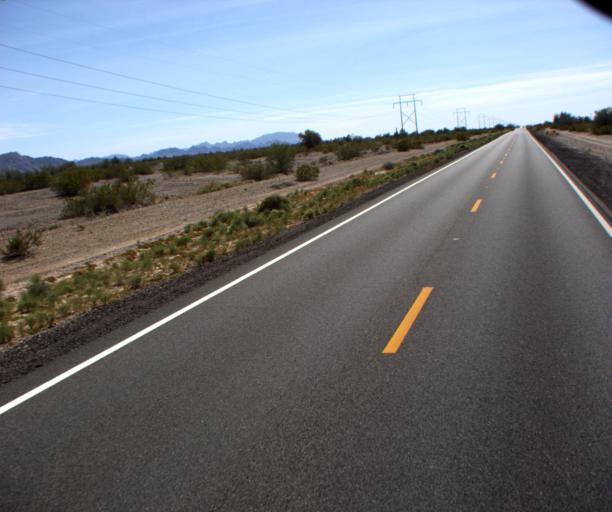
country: US
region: Arizona
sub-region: La Paz County
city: Quartzsite
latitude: 33.6383
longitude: -114.2171
